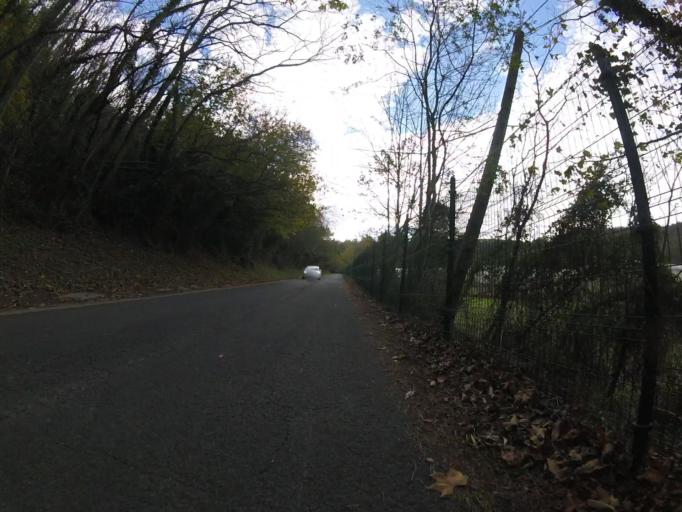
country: ES
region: Basque Country
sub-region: Provincia de Guipuzcoa
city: Errenteria
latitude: 43.2998
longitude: -1.9219
